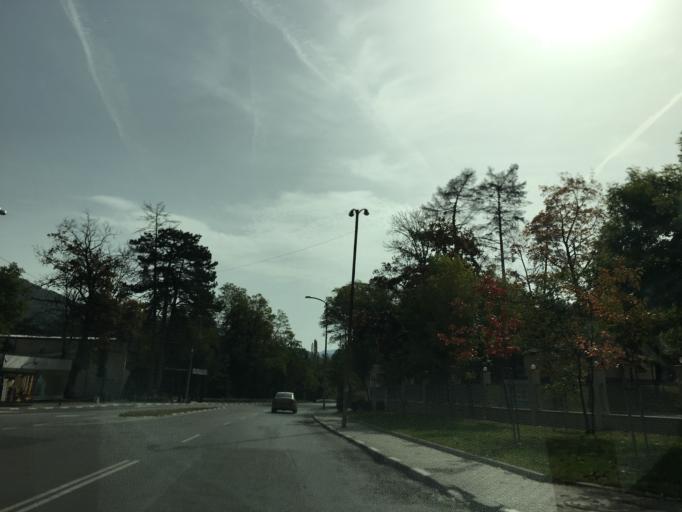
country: BG
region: Sofia-Capital
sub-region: Stolichna Obshtina
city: Sofia
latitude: 42.5955
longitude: 23.4146
